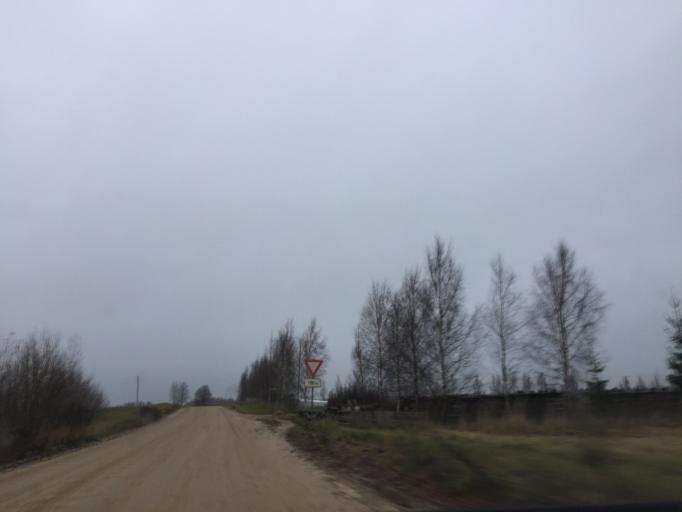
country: LV
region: Koceni
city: Koceni
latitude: 57.5490
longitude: 25.3205
